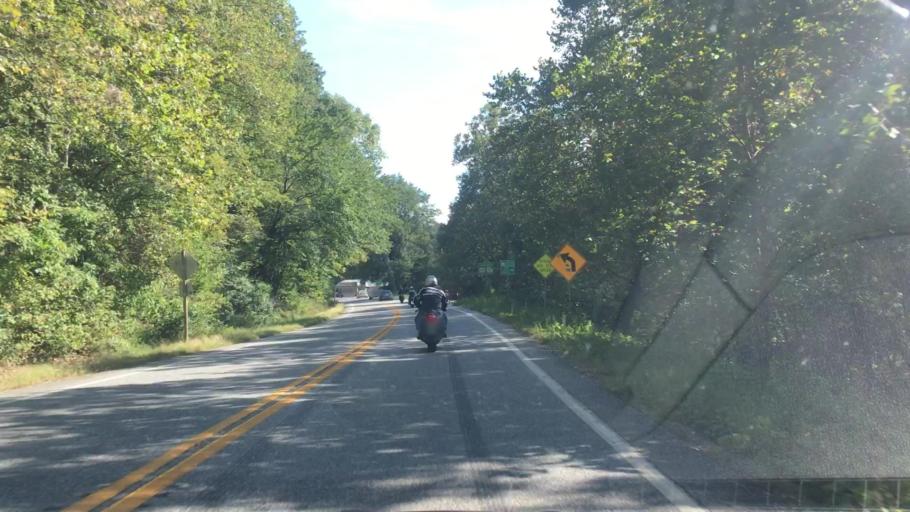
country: US
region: Georgia
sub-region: White County
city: Cleveland
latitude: 34.6652
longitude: -83.9020
